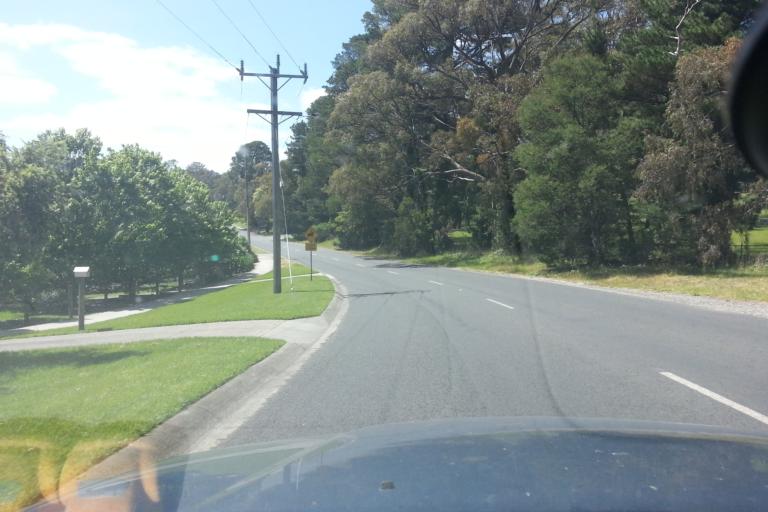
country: AU
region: Victoria
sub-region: Cardinia
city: Beaconsfield Upper
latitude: -38.0077
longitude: 145.4167
